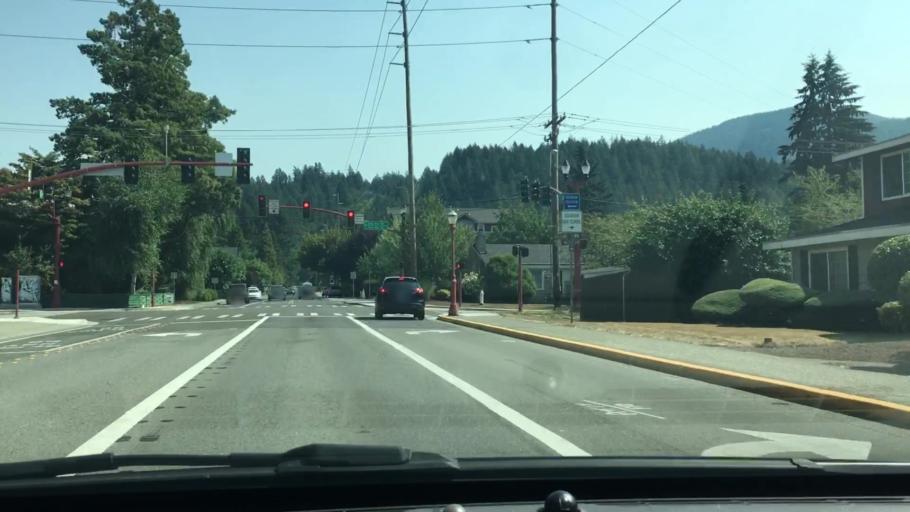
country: US
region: Washington
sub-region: King County
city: Issaquah
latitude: 47.5301
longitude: -122.0337
